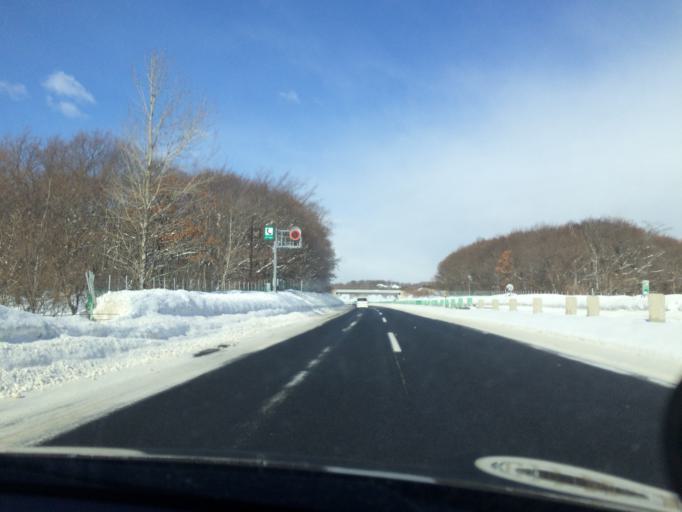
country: JP
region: Hokkaido
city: Kitahiroshima
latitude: 42.9160
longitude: 141.5475
